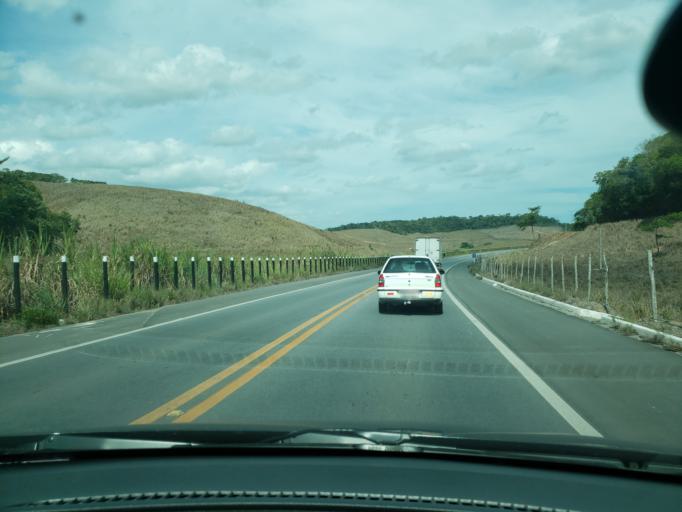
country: BR
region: Alagoas
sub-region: Murici
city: Murici
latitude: -9.3303
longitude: -35.9070
